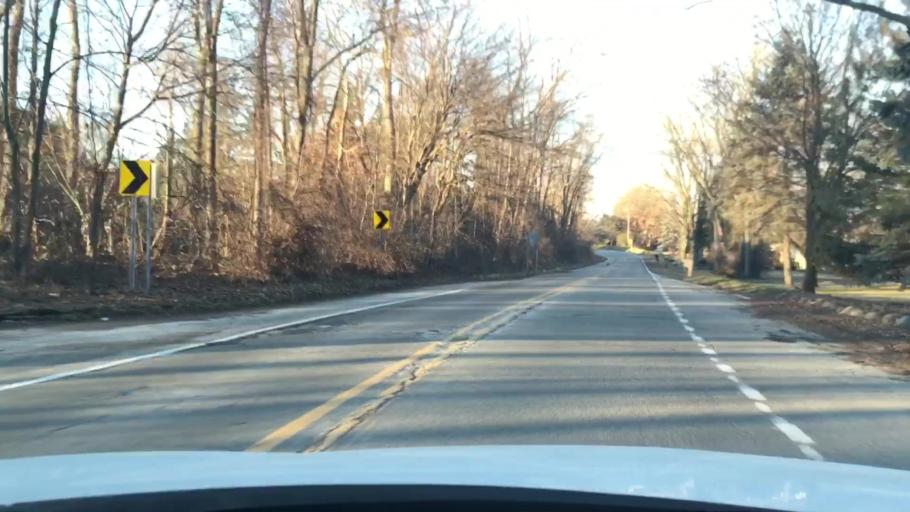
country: US
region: Michigan
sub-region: Oakland County
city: West Bloomfield Township
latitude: 42.5939
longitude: -83.4024
